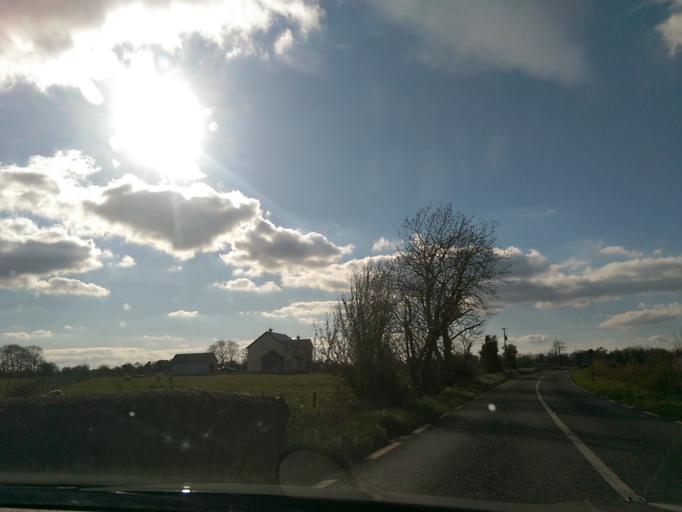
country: IE
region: Connaught
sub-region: County Galway
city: Loughrea
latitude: 53.2117
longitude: -8.4941
